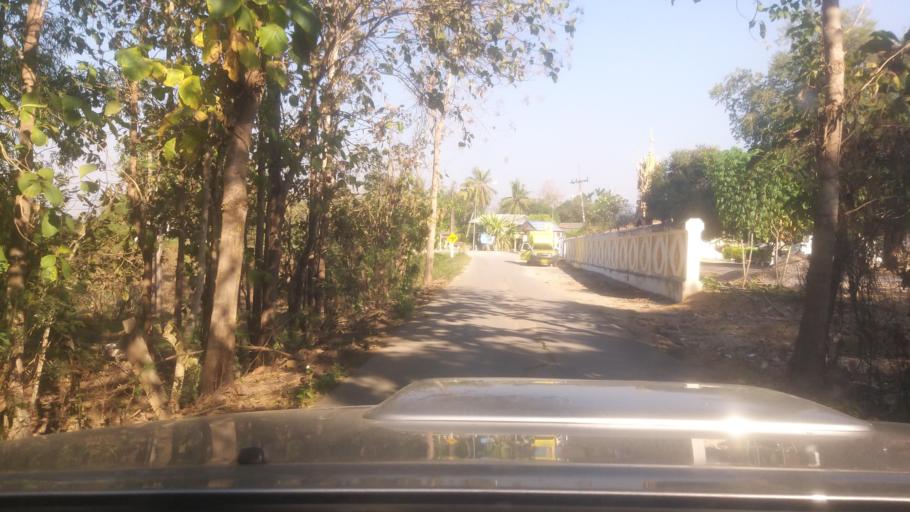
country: TH
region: Phrae
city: Phrae
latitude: 18.2636
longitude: 99.9906
